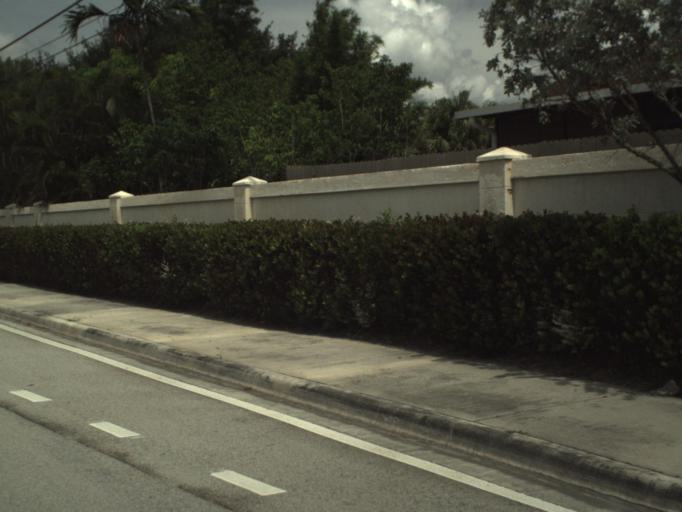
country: US
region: Florida
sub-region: Palm Beach County
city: Palm Beach Gardens
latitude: 26.8386
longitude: -80.1151
